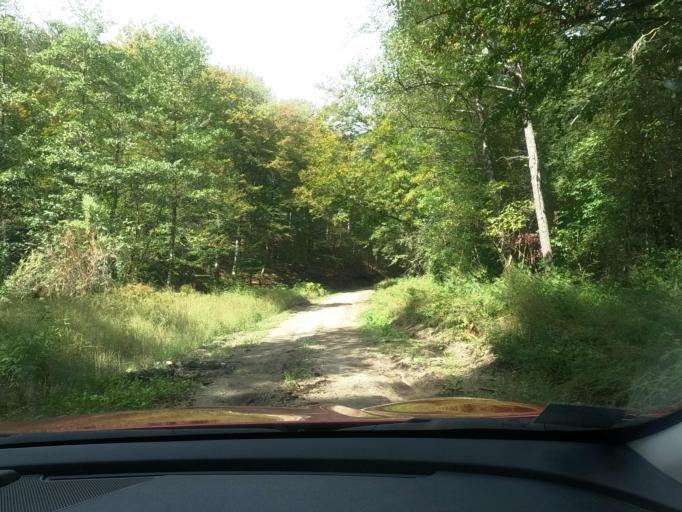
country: BA
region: Federation of Bosnia and Herzegovina
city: Velika Kladusa
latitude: 45.2384
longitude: 15.7754
